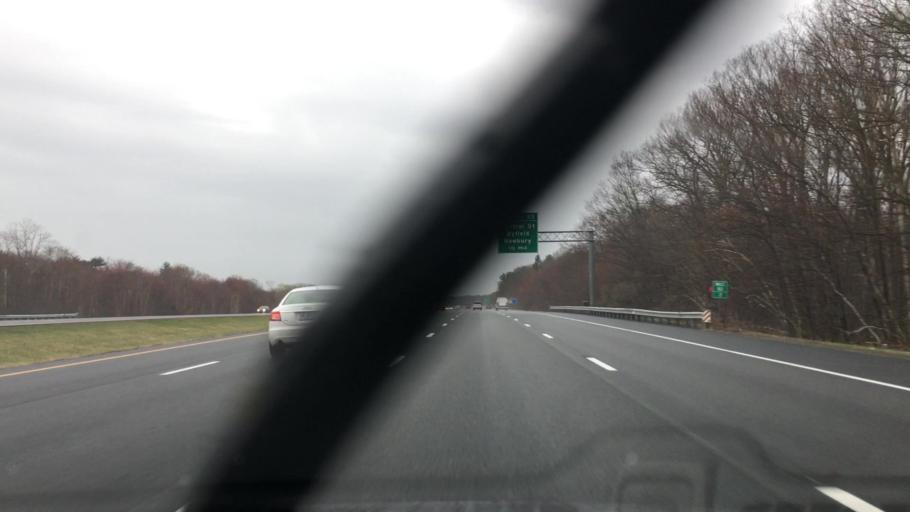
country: US
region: Massachusetts
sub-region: Essex County
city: West Newbury
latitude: 42.7653
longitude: -70.9363
